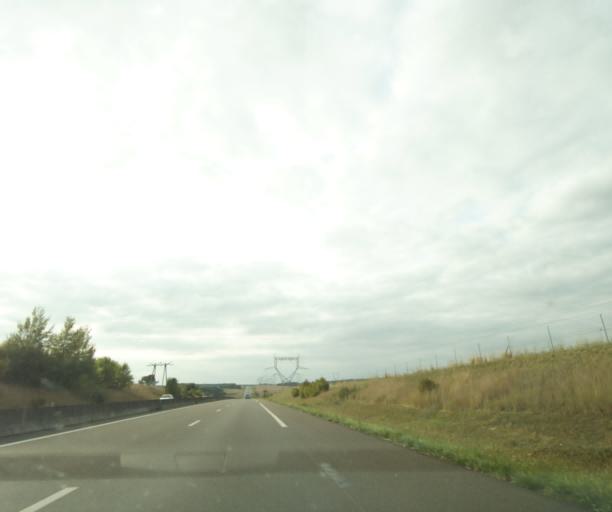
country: FR
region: Centre
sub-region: Departement d'Indre-et-Loire
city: Cerelles
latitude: 47.4823
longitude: 0.6831
